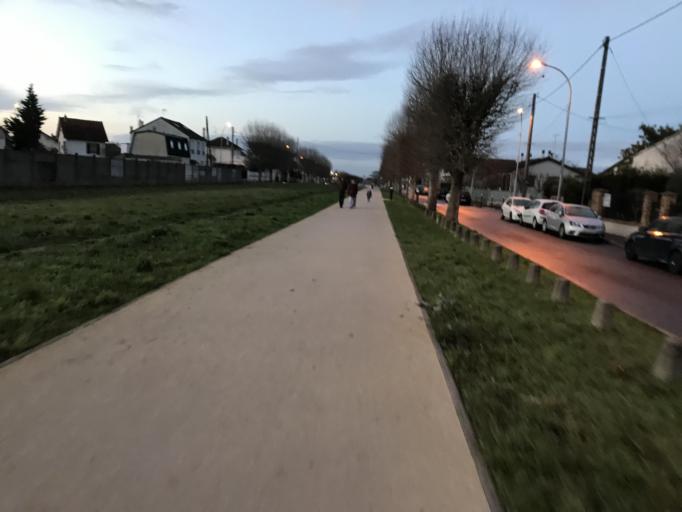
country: FR
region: Ile-de-France
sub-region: Departement de l'Essonne
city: Morangis
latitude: 48.6991
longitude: 2.3536
